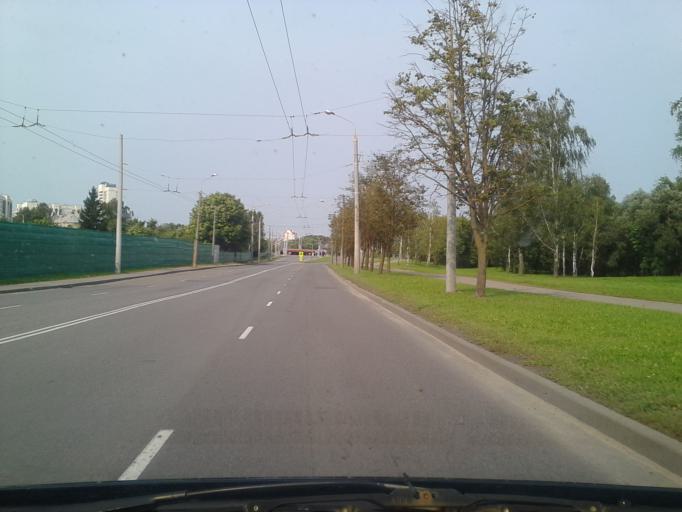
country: BY
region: Minsk
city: Novoye Medvezhino
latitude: 53.8662
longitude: 27.4959
